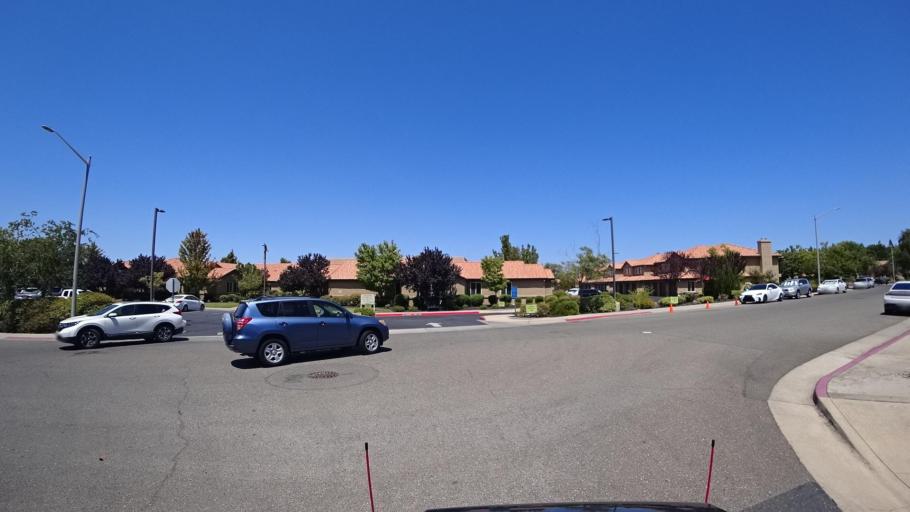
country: US
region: California
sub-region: Placer County
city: Rocklin
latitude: 38.8115
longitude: -121.2576
